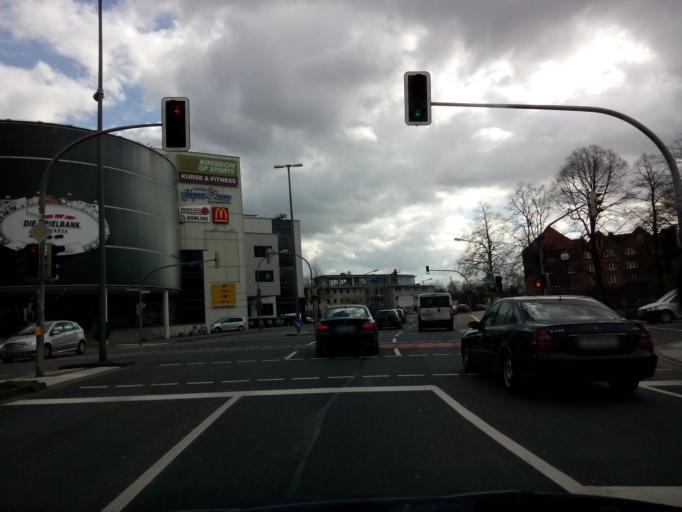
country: DE
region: Lower Saxony
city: Osnabrueck
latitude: 52.2724
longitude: 8.0576
